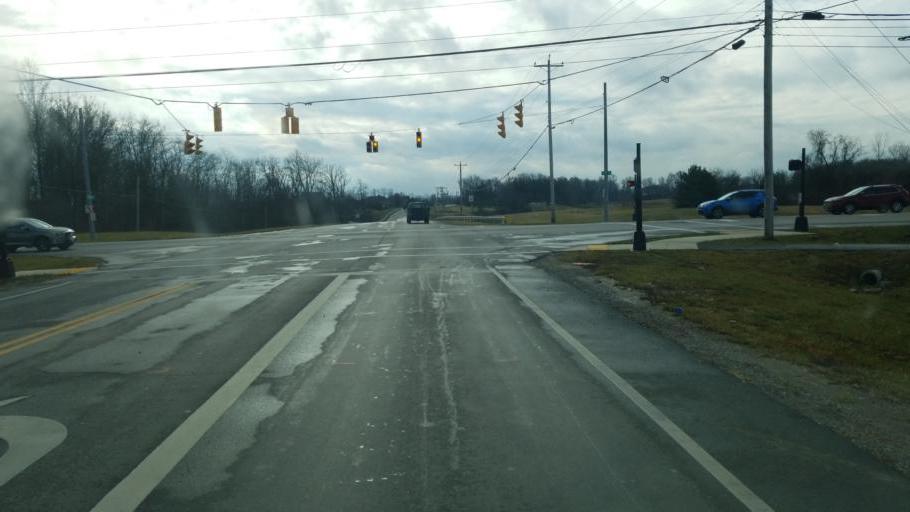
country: US
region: Ohio
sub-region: Delaware County
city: Powell
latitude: 40.1955
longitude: -83.0777
